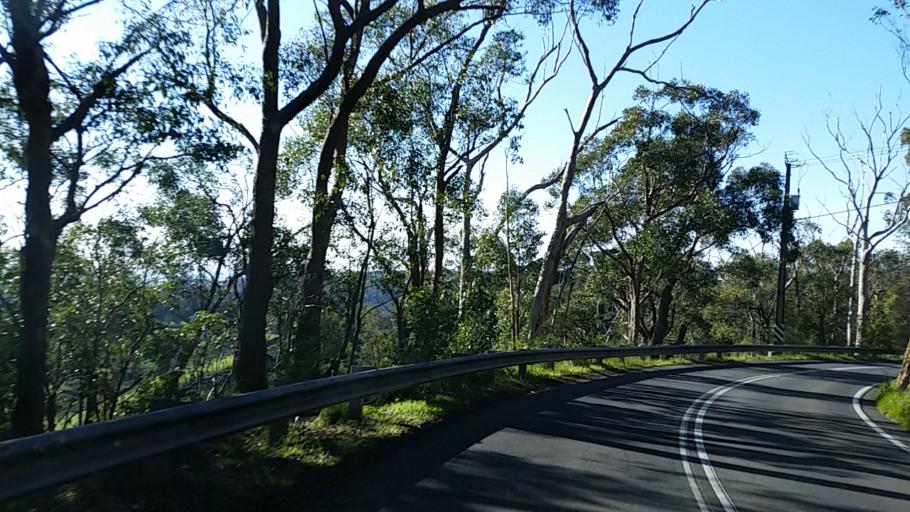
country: AU
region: South Australia
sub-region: Adelaide Hills
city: Adelaide Hills
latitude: -34.9333
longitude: 138.7312
